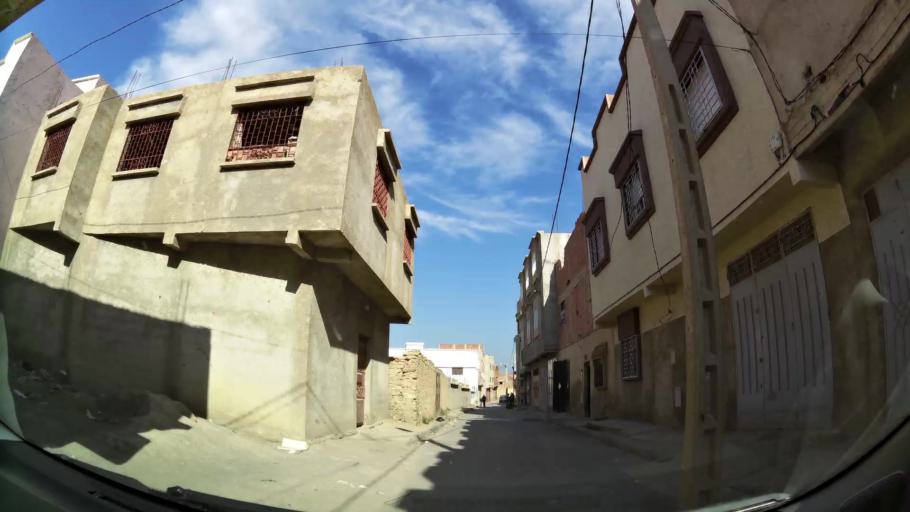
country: MA
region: Oriental
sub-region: Oujda-Angad
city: Oujda
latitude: 34.7213
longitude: -1.8856
